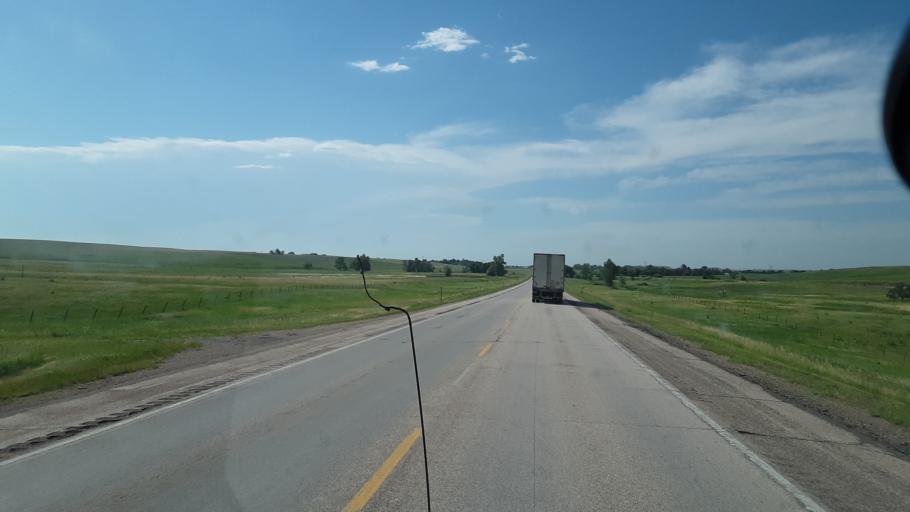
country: US
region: South Dakota
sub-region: Lawrence County
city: Deadwood
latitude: 44.5215
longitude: -103.6936
